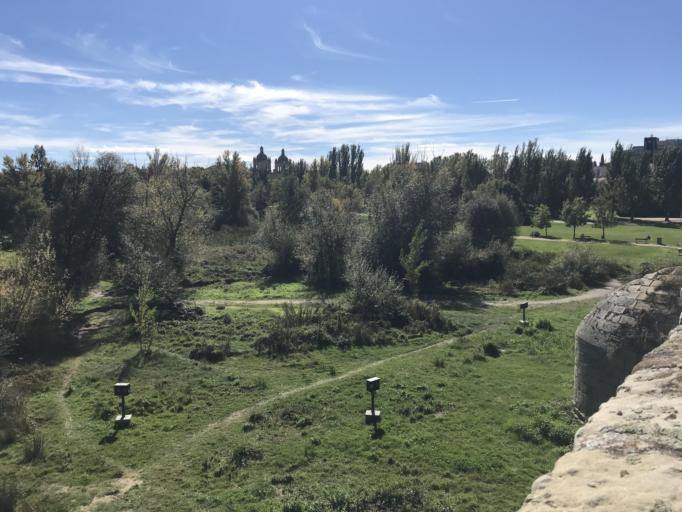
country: ES
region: Castille and Leon
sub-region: Provincia de Salamanca
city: Salamanca
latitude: 40.9575
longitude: -5.6702
